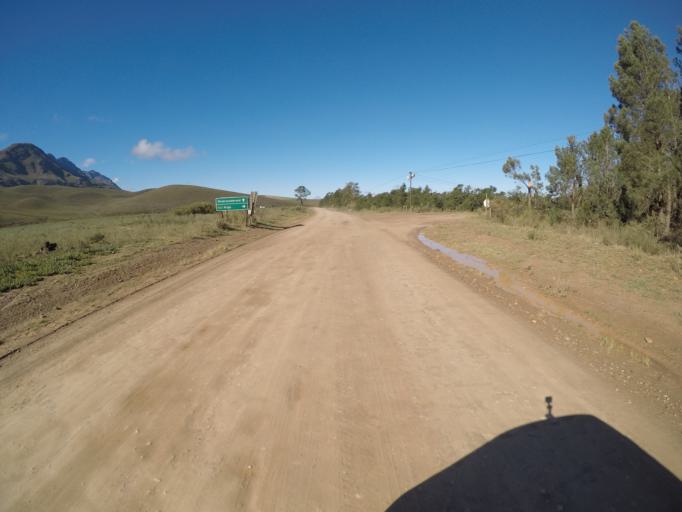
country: ZA
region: Western Cape
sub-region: Overberg District Municipality
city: Caledon
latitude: -34.0541
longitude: 19.6152
